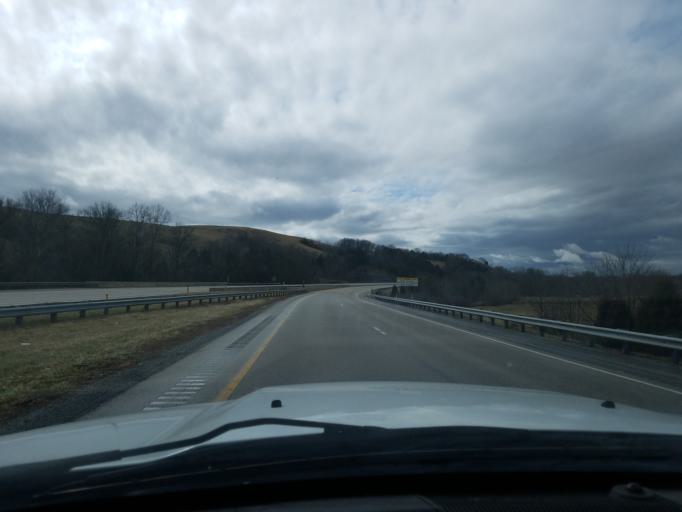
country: US
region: Kentucky
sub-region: Bath County
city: Owingsville
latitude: 38.1134
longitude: -83.8050
